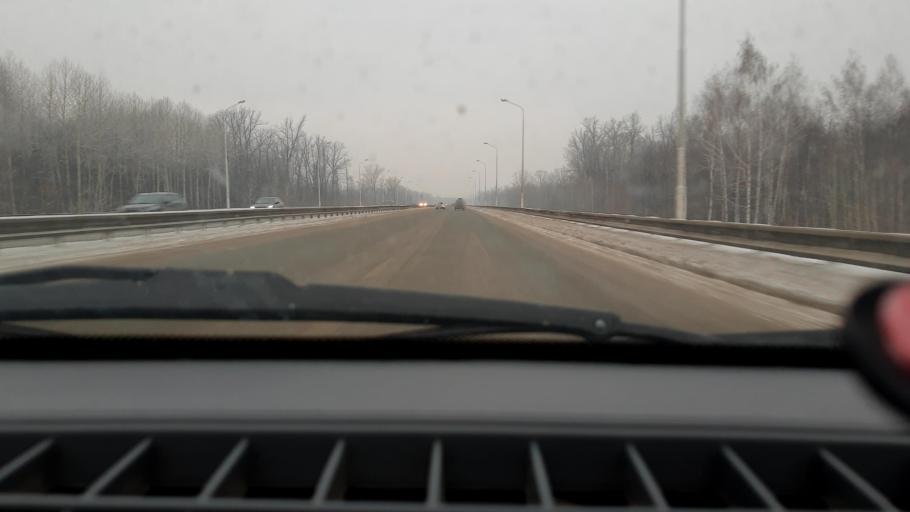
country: RU
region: Bashkortostan
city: Ufa
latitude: 54.6697
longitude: 56.0493
